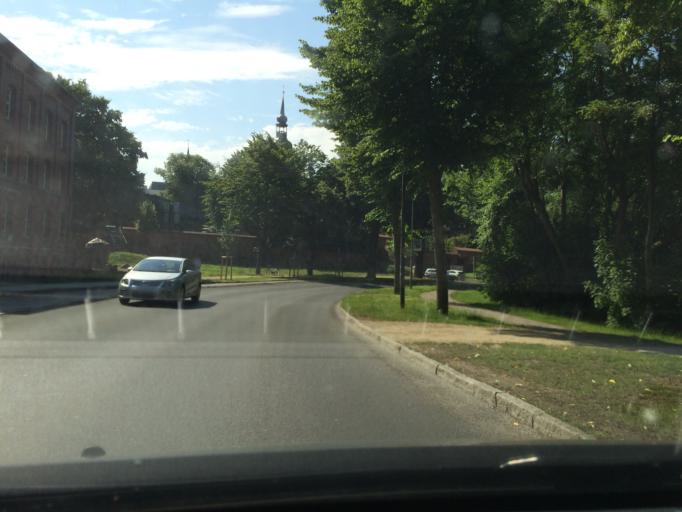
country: DE
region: Mecklenburg-Vorpommern
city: Stralsund
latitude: 54.3131
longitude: 13.0859
